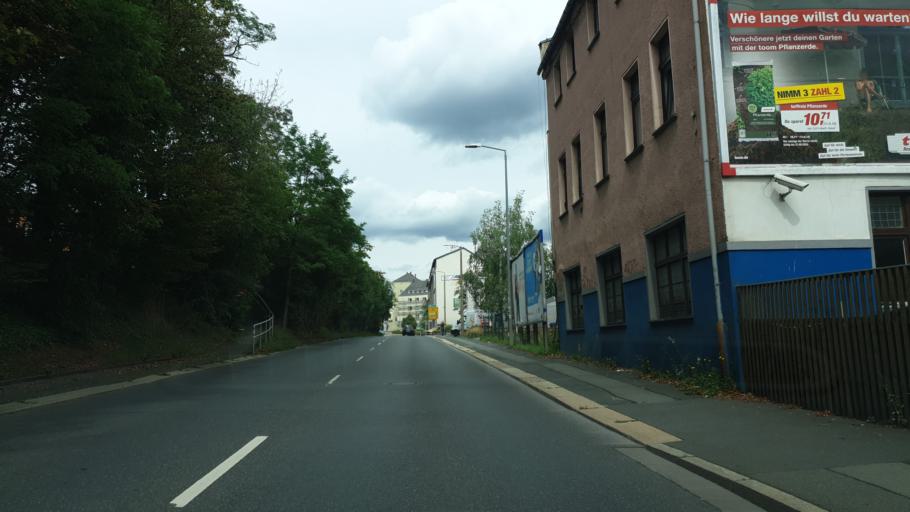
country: DE
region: Saxony
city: Plauen
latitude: 50.4971
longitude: 12.1435
